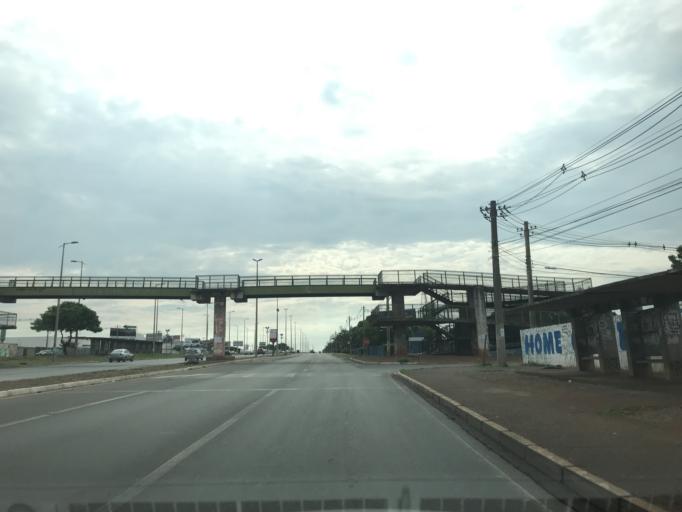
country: BR
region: Federal District
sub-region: Brasilia
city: Brasilia
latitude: -15.8076
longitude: -47.9667
